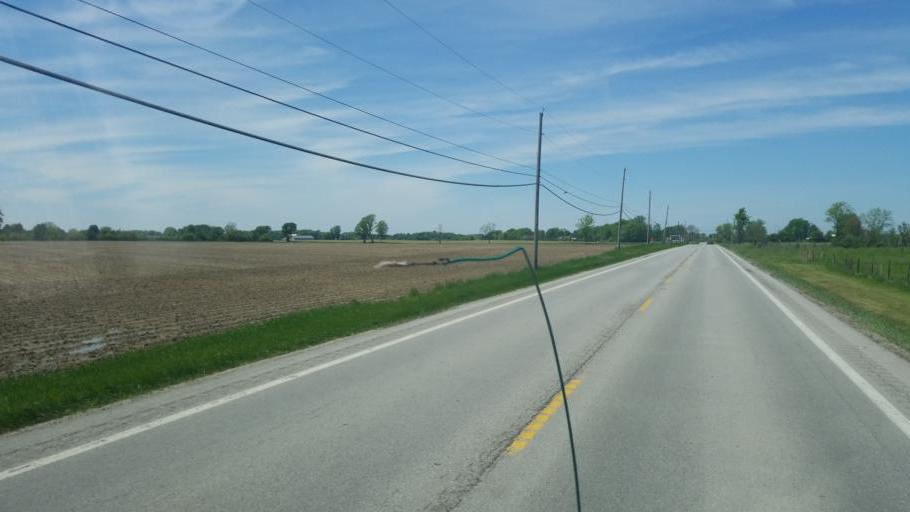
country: US
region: Ohio
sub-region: Huron County
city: Norwalk
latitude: 41.1992
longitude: -82.5789
